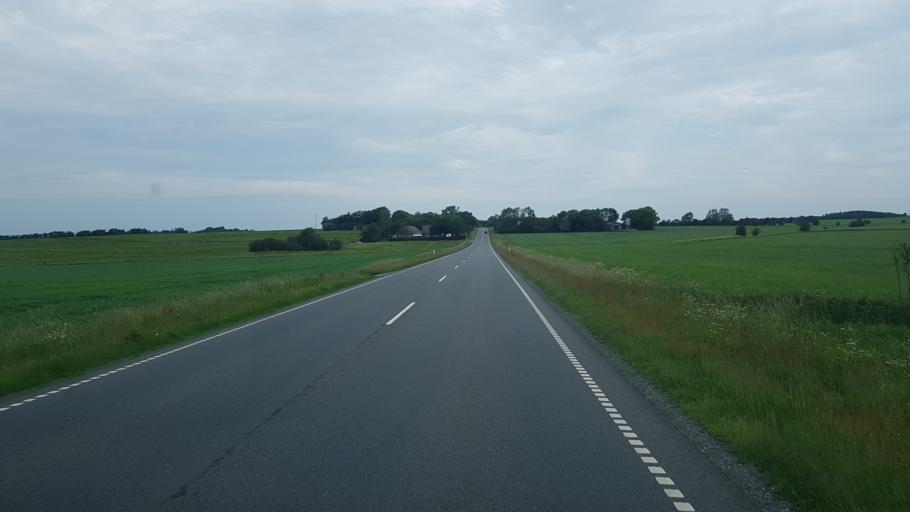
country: DK
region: South Denmark
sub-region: Vejen Kommune
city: Rodding
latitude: 55.4135
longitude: 9.0284
